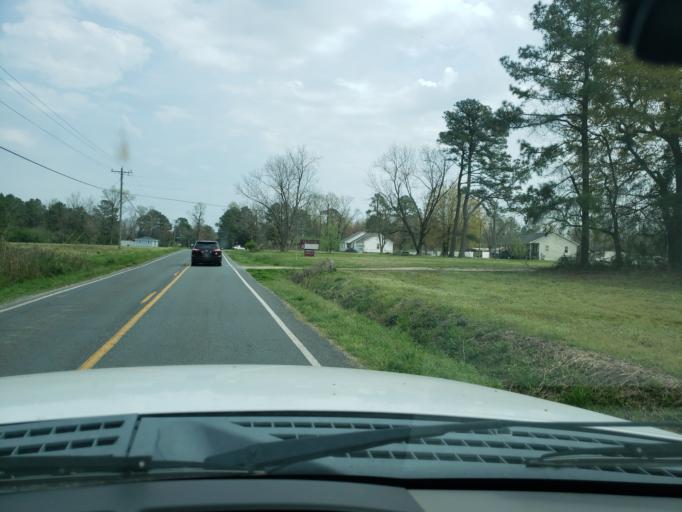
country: US
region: North Carolina
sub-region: Duplin County
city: Beulaville
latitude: 34.7799
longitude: -77.8327
